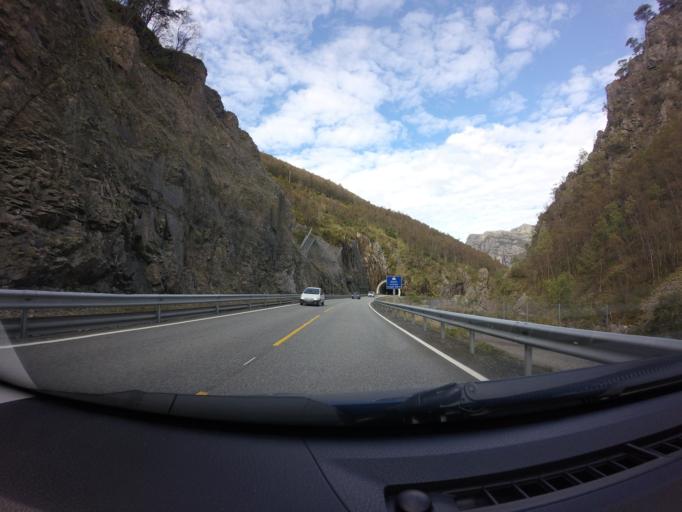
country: NO
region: Rogaland
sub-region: Forsand
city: Forsand
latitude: 58.7918
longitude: 6.2765
